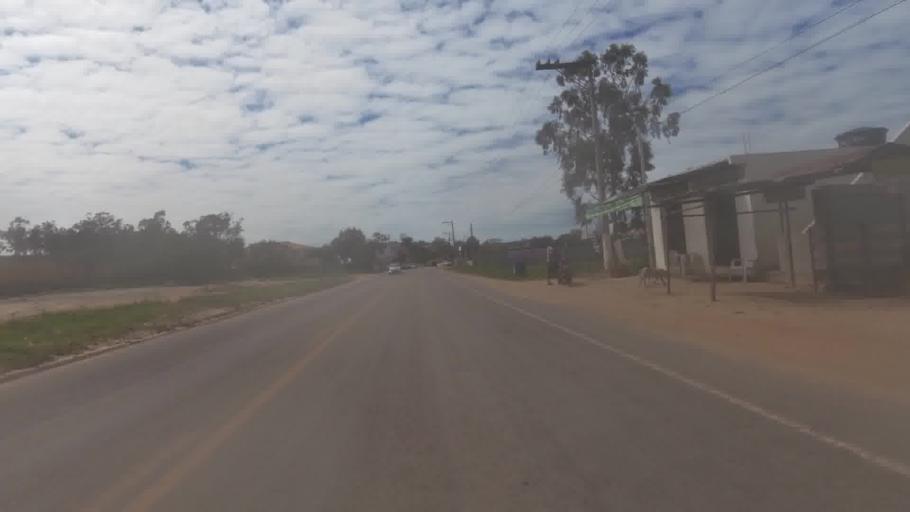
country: BR
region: Espirito Santo
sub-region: Marataizes
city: Marataizes
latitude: -21.2003
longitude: -40.9644
